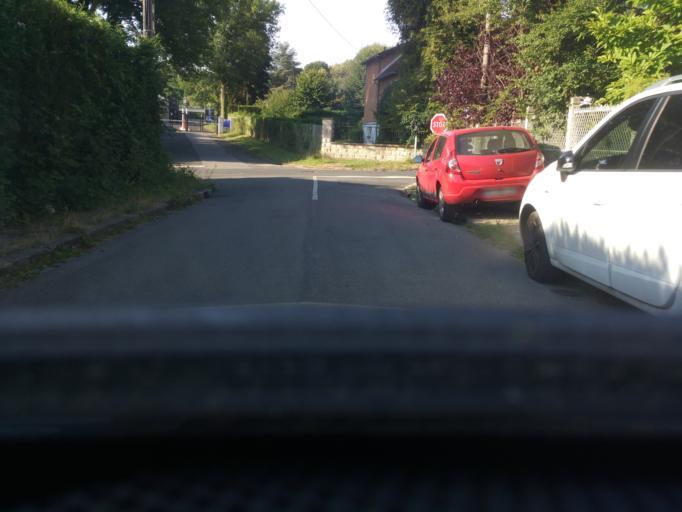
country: FR
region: Ile-de-France
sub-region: Departement des Yvelines
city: Saint-Remy-les-Chevreuse
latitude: 48.6953
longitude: 2.0611
